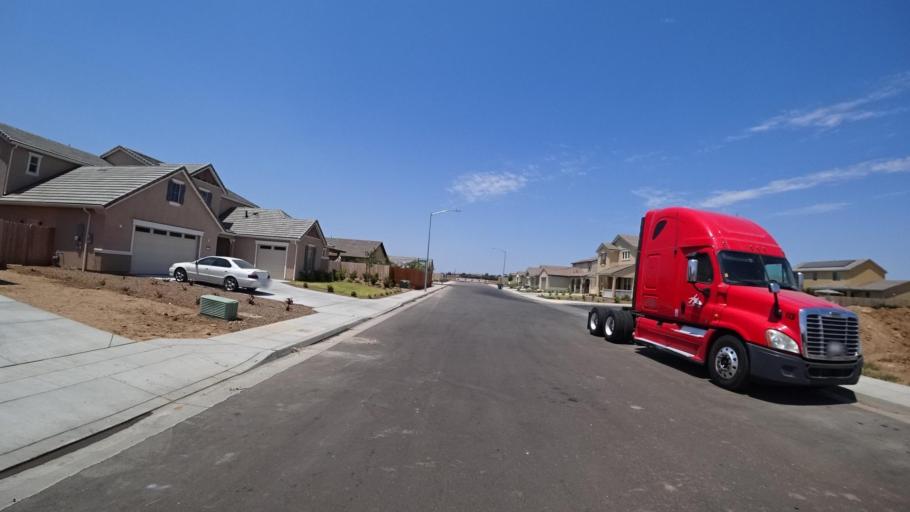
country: US
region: California
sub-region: Fresno County
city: Tarpey Village
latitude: 36.7761
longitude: -119.6582
